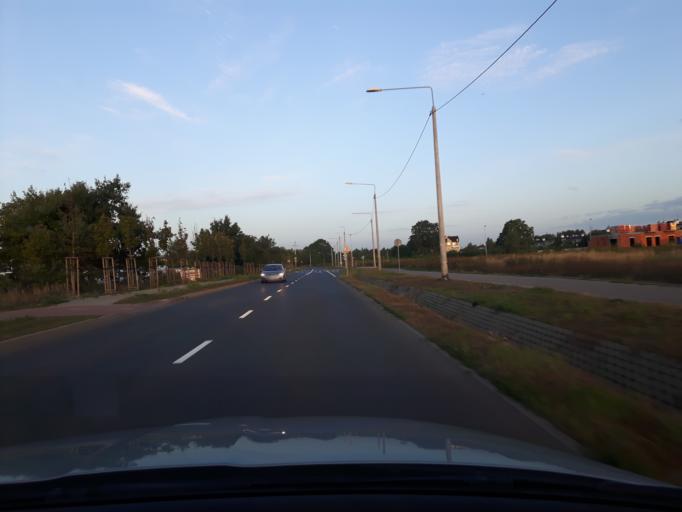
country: PL
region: Masovian Voivodeship
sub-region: Warszawa
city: Wawer
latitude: 52.1865
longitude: 21.1510
